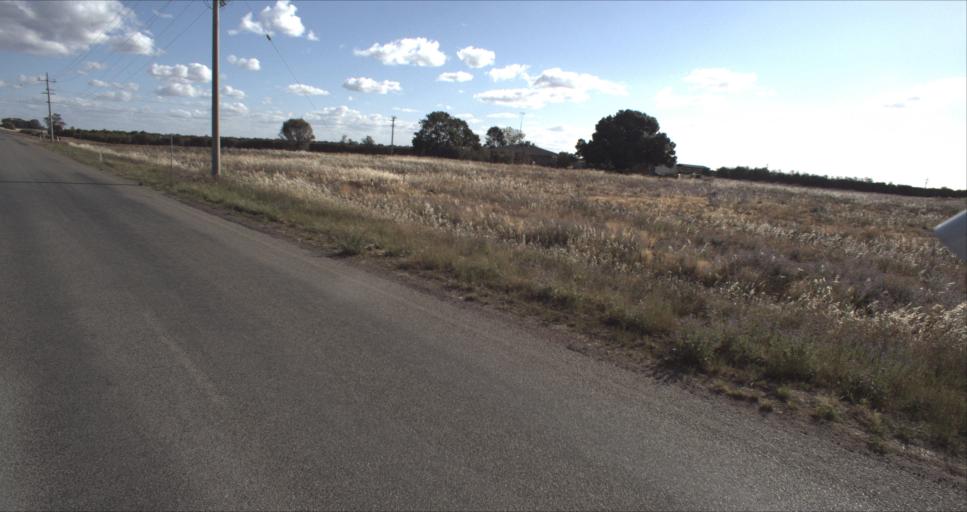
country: AU
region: New South Wales
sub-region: Leeton
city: Leeton
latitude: -34.5266
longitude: 146.2823
